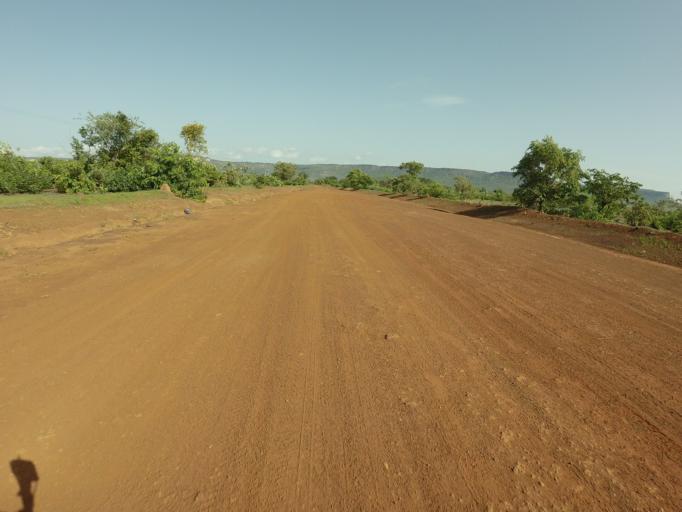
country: GH
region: Upper East
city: Bawku
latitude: 10.6839
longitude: -0.2150
